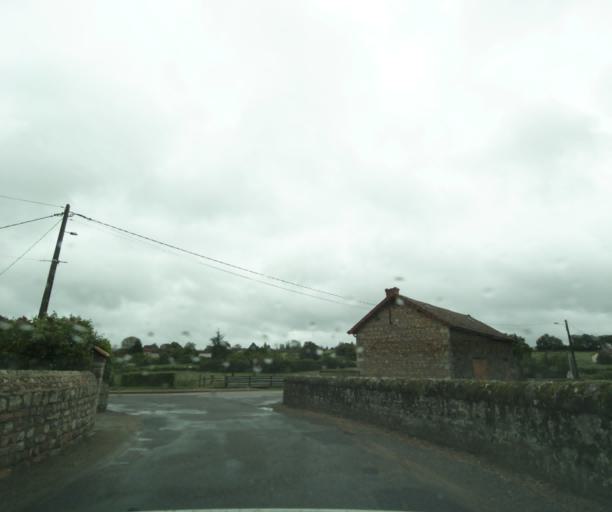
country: FR
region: Bourgogne
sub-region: Departement de Saone-et-Loire
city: Charolles
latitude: 46.4799
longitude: 4.4390
